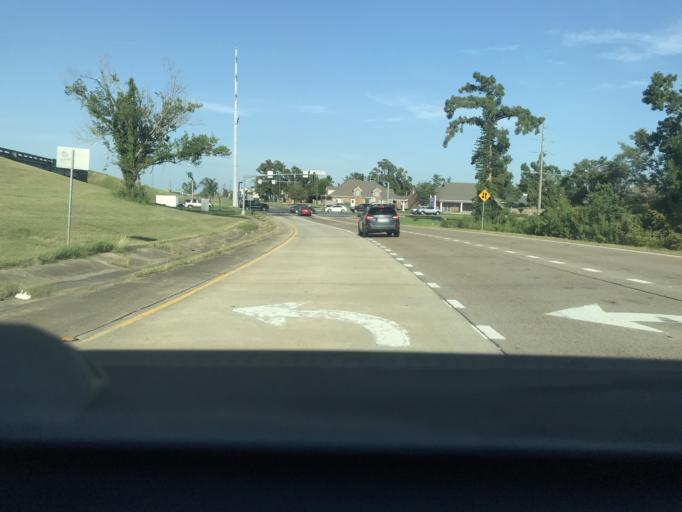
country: US
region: Louisiana
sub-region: Calcasieu Parish
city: Lake Charles
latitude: 30.1966
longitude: -93.2335
